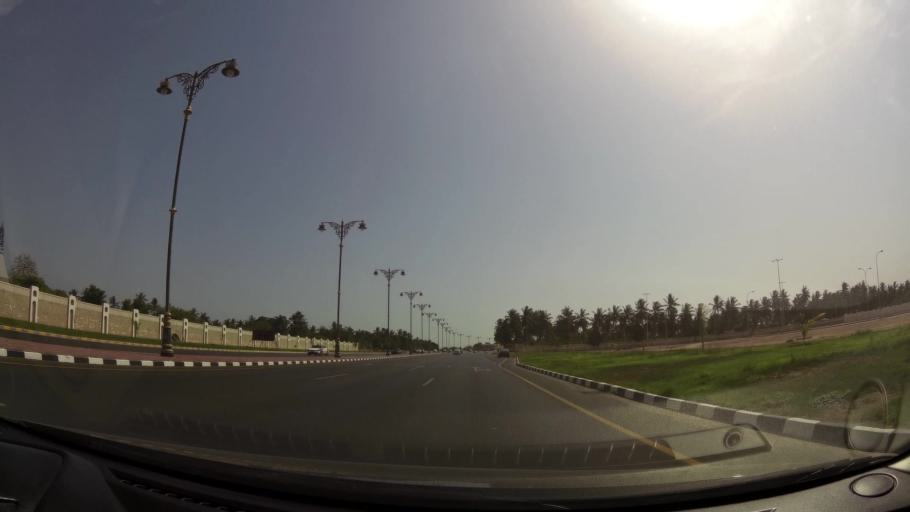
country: OM
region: Zufar
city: Salalah
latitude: 17.0260
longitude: 54.1254
